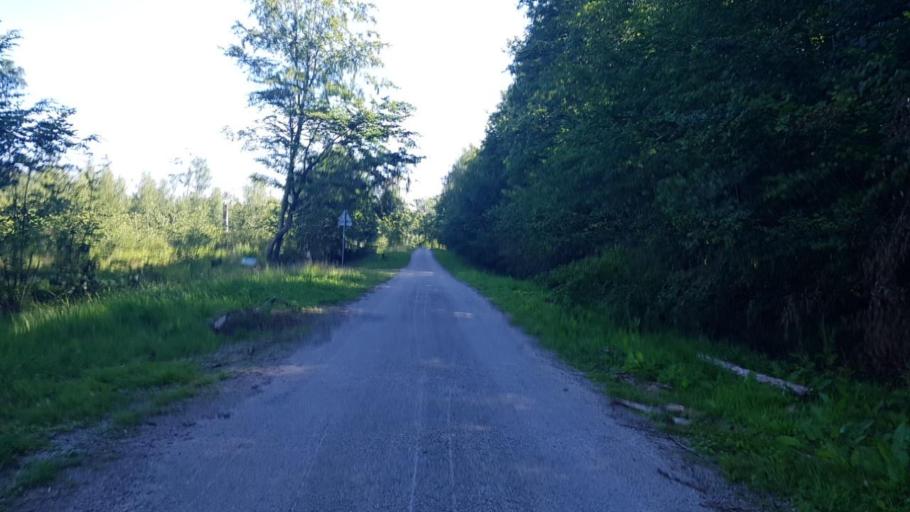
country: FR
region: Picardie
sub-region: Departement de l'Aisne
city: Hirson
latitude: 49.9416
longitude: 4.0970
